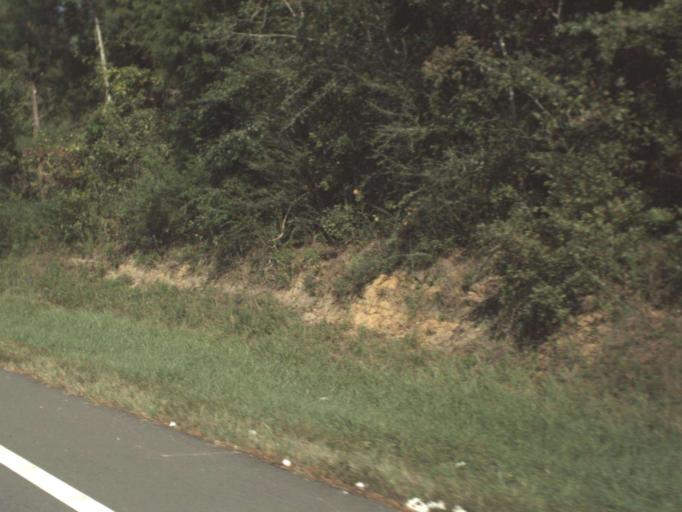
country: US
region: Alabama
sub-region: Covington County
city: Florala
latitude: 30.9886
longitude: -86.3399
